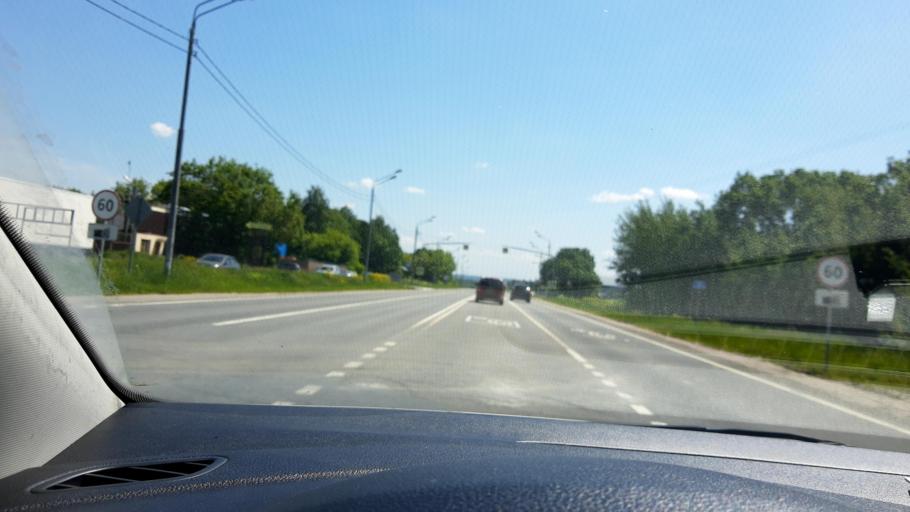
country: RU
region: Moskovskaya
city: Bronnitsy
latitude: 55.4752
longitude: 38.1872
